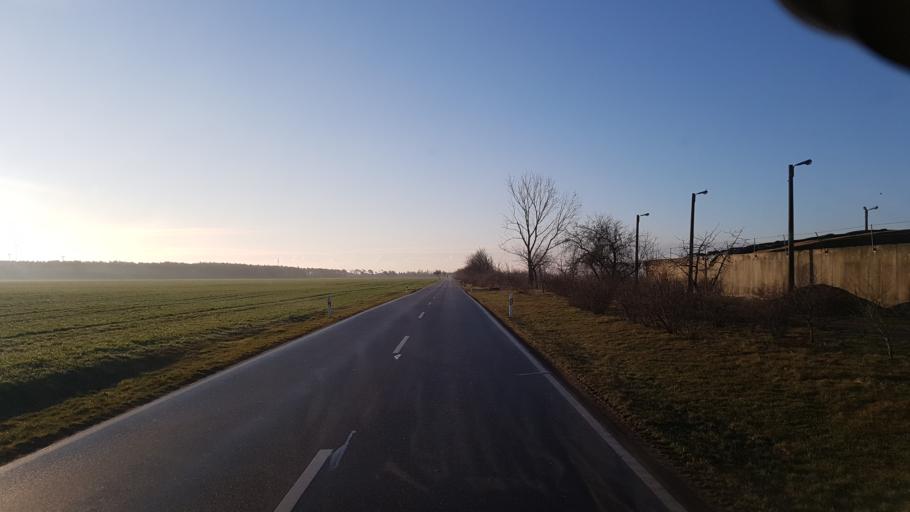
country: DE
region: Saxony
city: Arzberg
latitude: 51.5339
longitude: 13.1748
